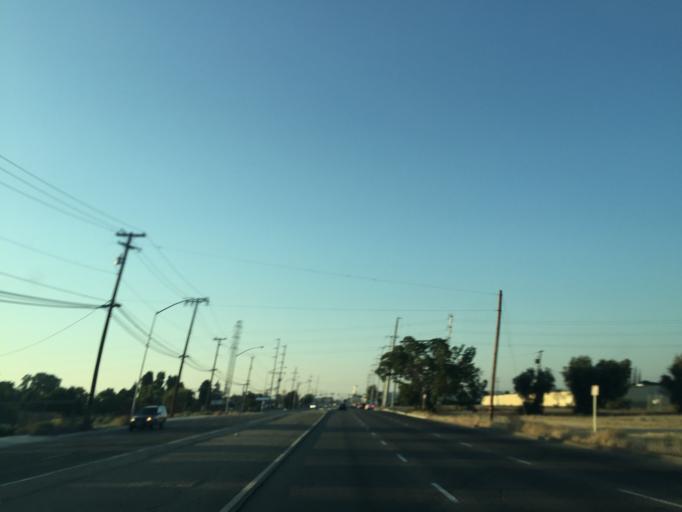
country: US
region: California
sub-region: Fresno County
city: Sunnyside
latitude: 36.7470
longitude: -119.7001
